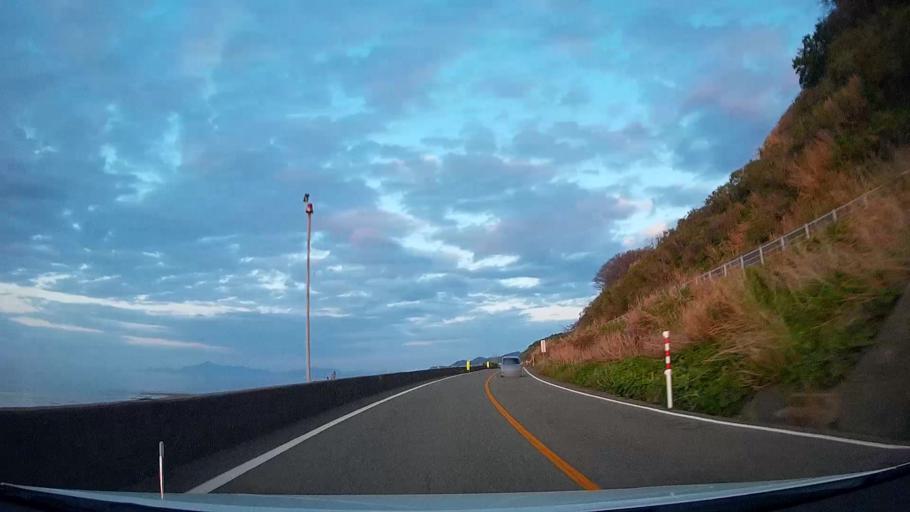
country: JP
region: Niigata
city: Joetsu
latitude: 37.1721
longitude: 138.1102
